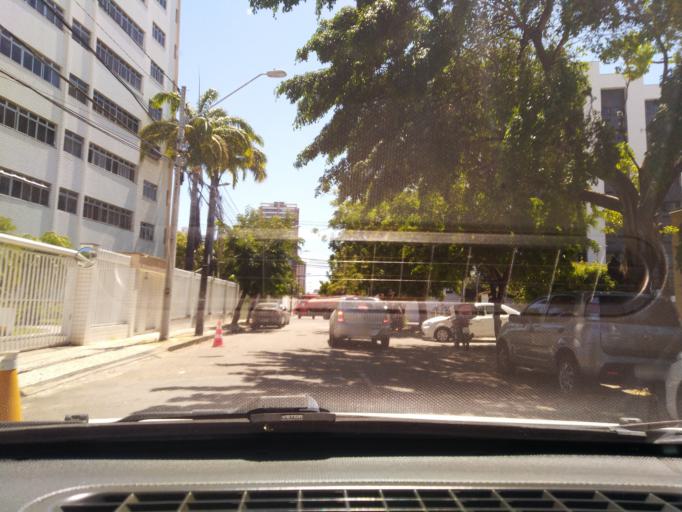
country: BR
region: Ceara
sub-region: Fortaleza
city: Fortaleza
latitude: -3.7432
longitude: -38.4797
